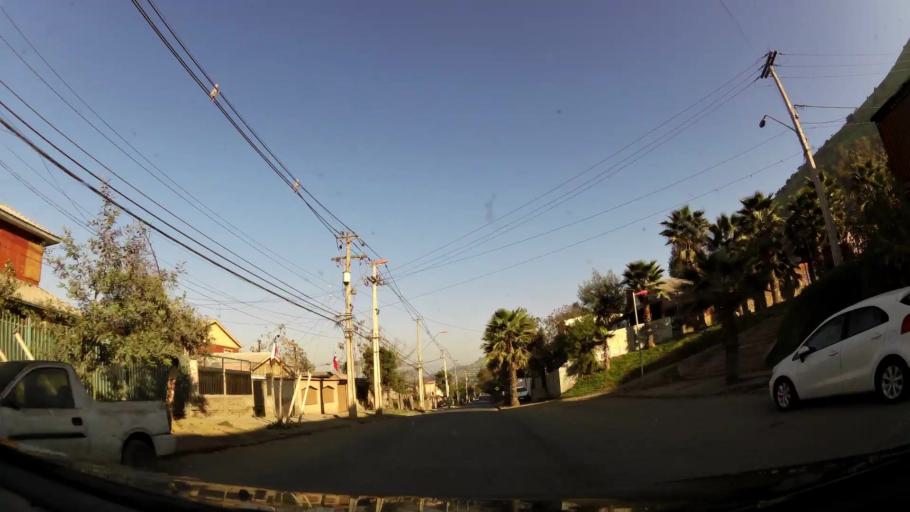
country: CL
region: Santiago Metropolitan
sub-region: Provincia de Santiago
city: Santiago
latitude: -33.3770
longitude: -70.6222
